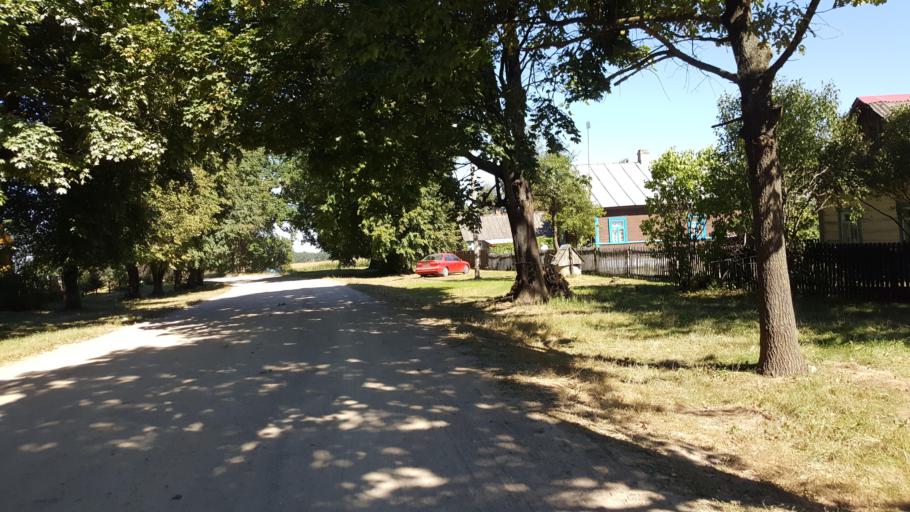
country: PL
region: Lublin Voivodeship
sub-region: Powiat bialski
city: Rokitno
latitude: 52.2145
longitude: 23.3970
